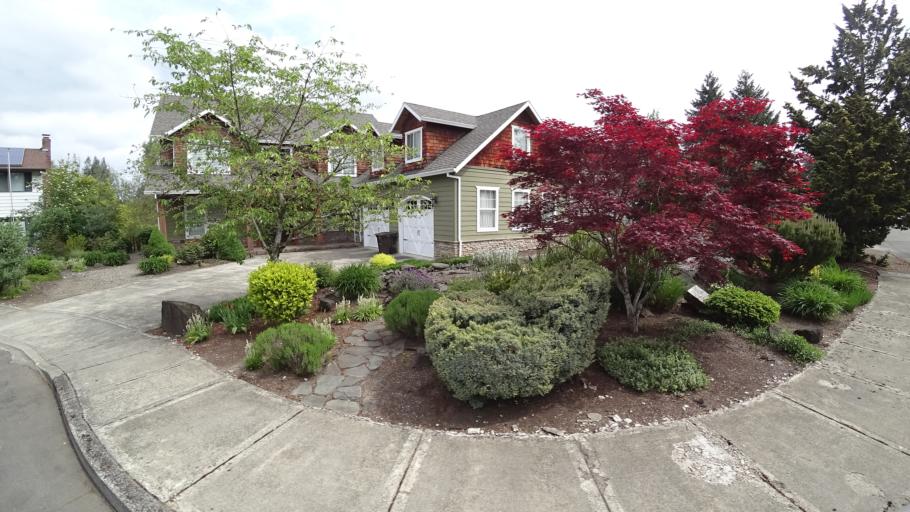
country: US
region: Oregon
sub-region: Washington County
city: Hillsboro
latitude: 45.5323
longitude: -122.9971
